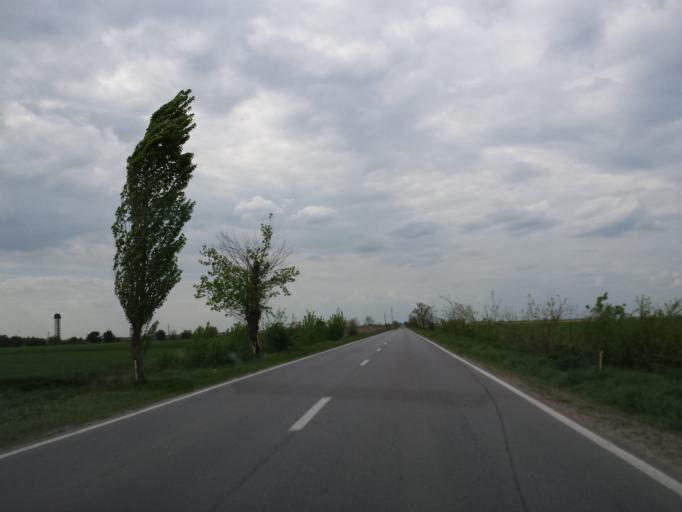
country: RO
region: Timis
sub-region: Comuna Sanpetru Mare
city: Sanpetru Mare
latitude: 46.0339
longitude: 20.6583
